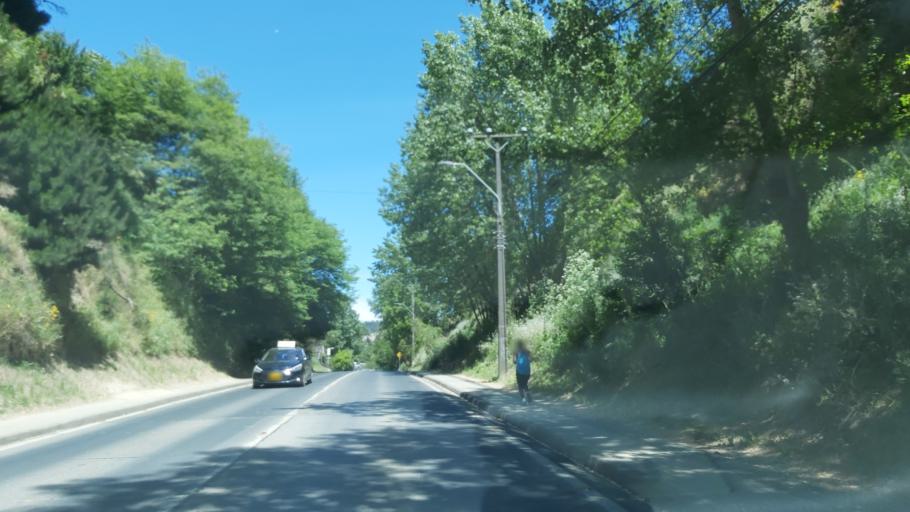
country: CL
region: Maule
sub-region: Provincia de Talca
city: Constitucion
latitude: -35.3289
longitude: -72.4197
